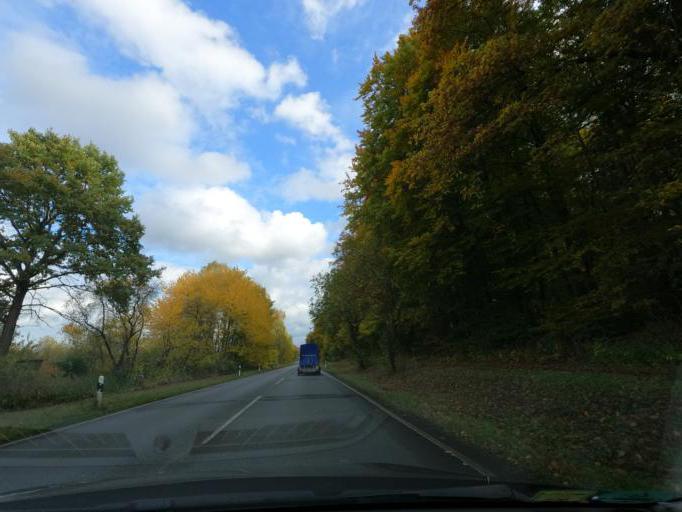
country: DE
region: Lower Saxony
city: Wolfenbuettel
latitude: 52.1540
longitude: 10.5012
